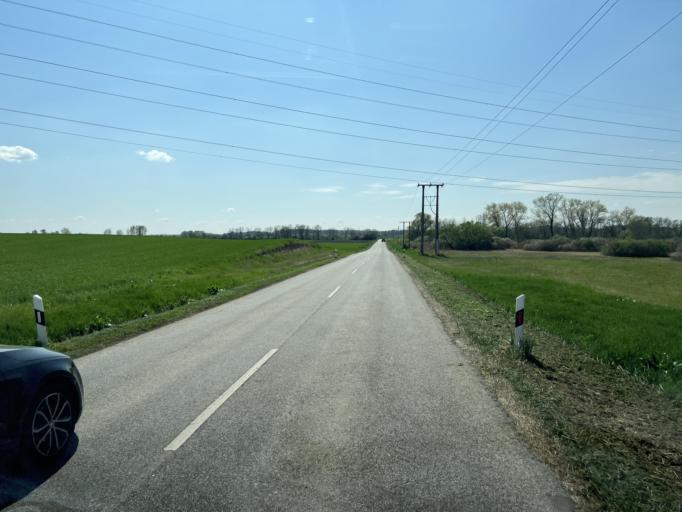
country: HU
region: Pest
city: Inarcs
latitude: 47.2326
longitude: 19.3074
